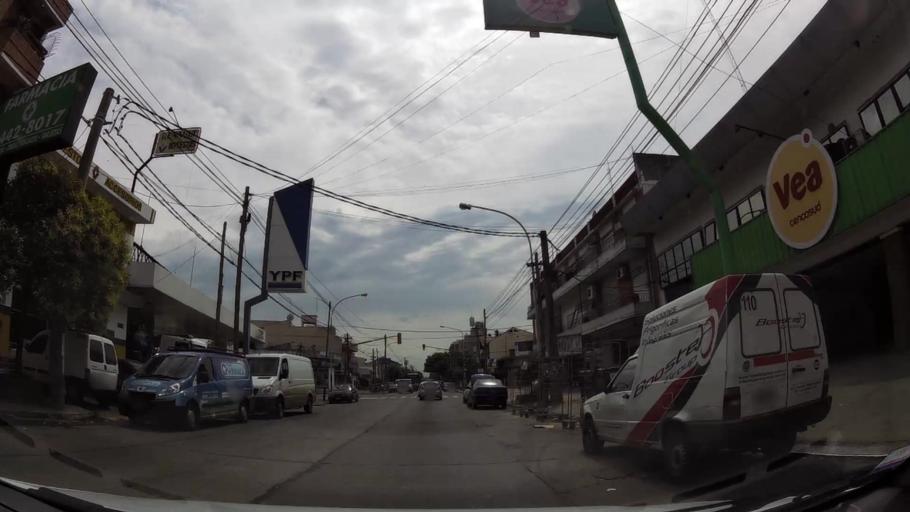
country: AR
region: Buenos Aires F.D.
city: Villa Lugano
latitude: -34.6923
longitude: -58.5005
